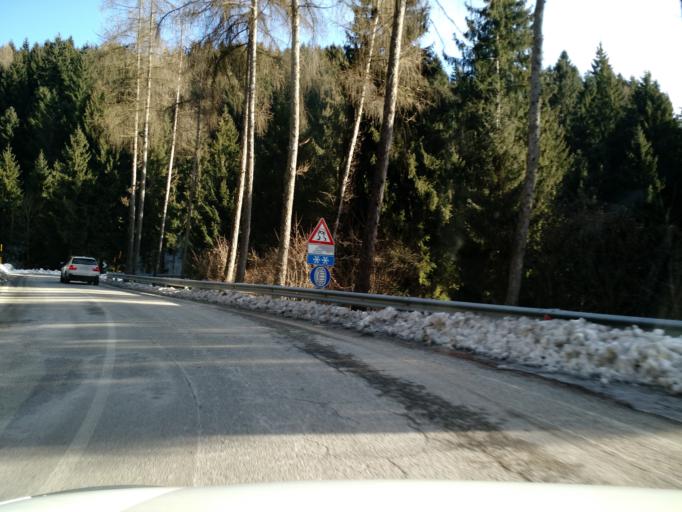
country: IT
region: Veneto
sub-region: Provincia di Vicenza
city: Canove di Roana
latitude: 45.8752
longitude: 11.4788
